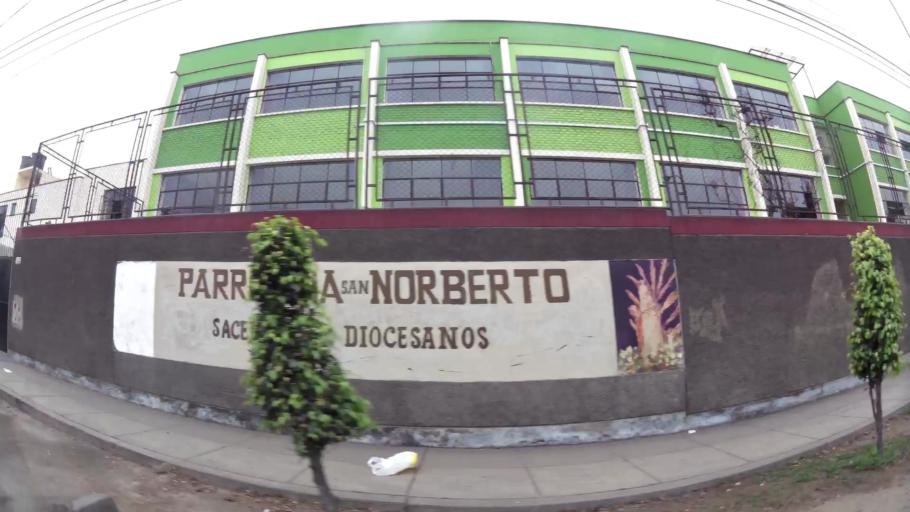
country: PE
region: Lima
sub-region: Lima
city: San Luis
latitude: -12.0852
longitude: -77.0177
